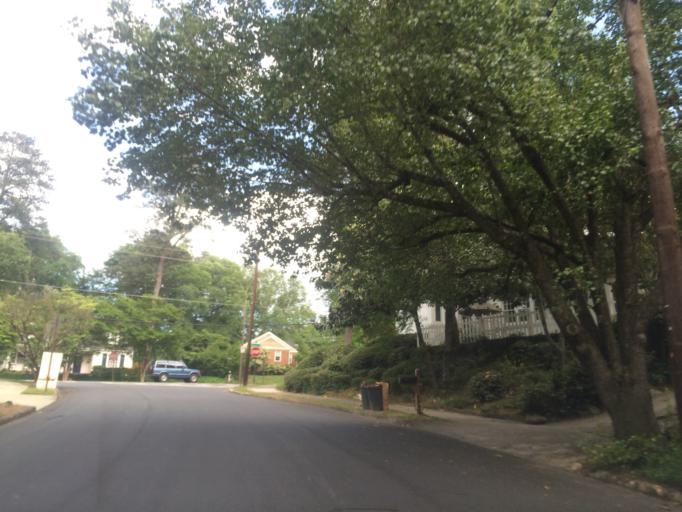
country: US
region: Georgia
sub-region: DeKalb County
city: Druid Hills
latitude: 33.7985
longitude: -84.3504
